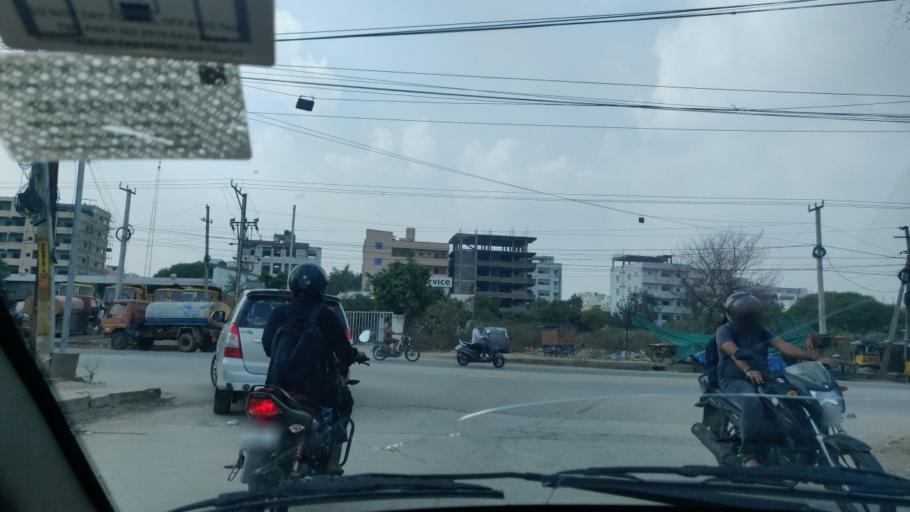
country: IN
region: Telangana
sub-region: Rangareddi
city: Kukatpalli
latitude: 17.4528
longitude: 78.3972
